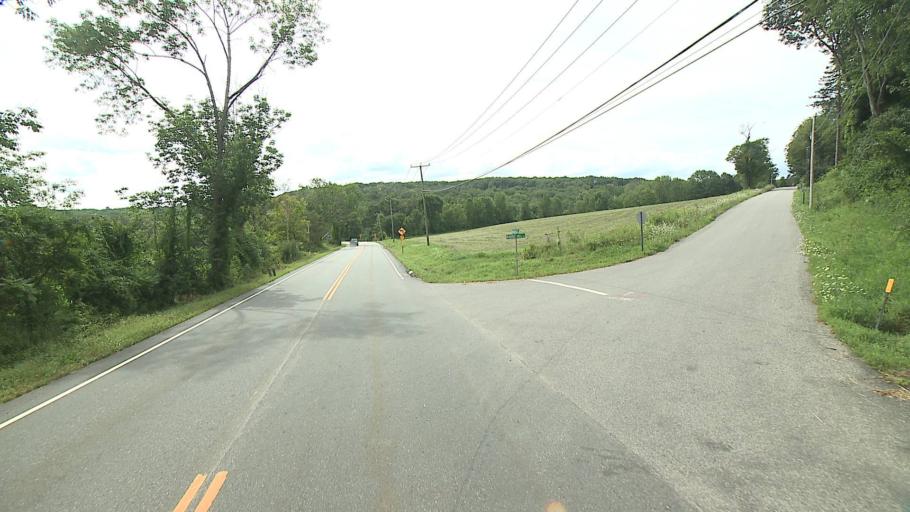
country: US
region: Connecticut
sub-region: Litchfield County
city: New Preston
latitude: 41.7171
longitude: -73.3283
